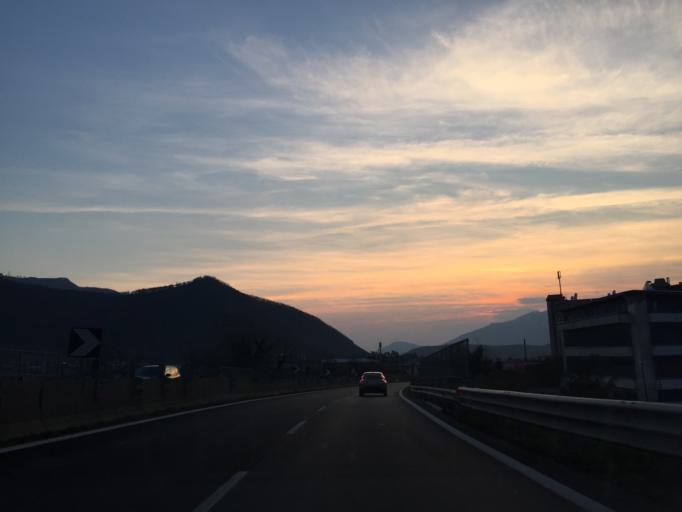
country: IT
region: Campania
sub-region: Provincia di Avellino
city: Solofra
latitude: 40.8345
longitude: 14.8376
